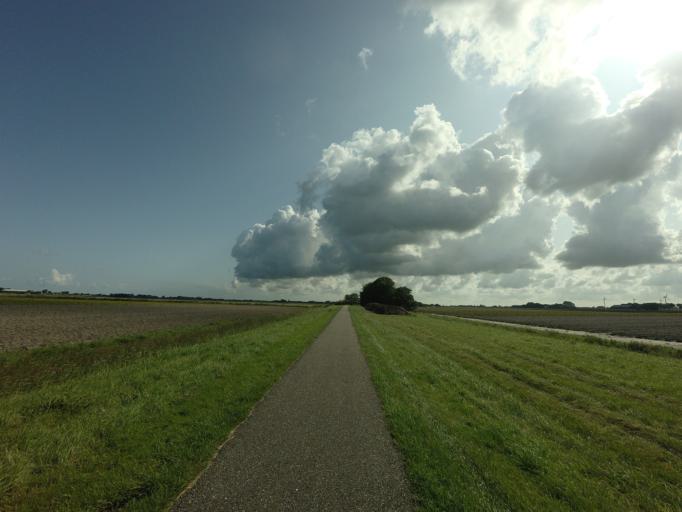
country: NL
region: Friesland
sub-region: Gemeente Franekeradeel
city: Tzummarum
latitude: 53.2628
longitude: 5.5539
